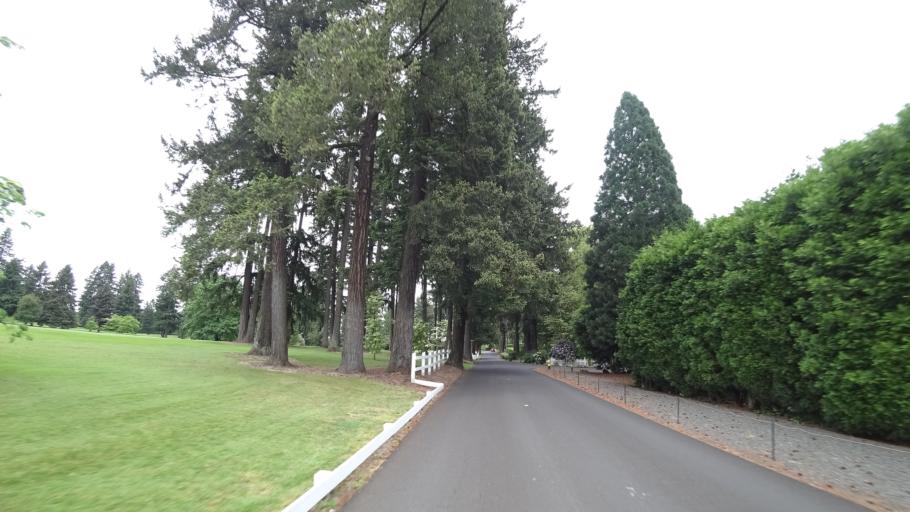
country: US
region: Oregon
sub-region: Clackamas County
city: Milwaukie
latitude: 45.4528
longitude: -122.6500
